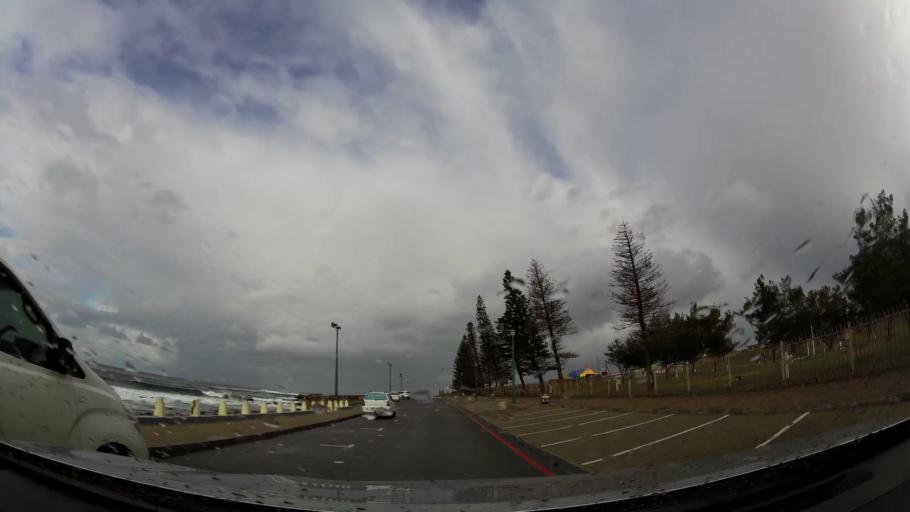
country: ZA
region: Western Cape
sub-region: Eden District Municipality
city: Mossel Bay
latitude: -34.1838
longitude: 22.1580
